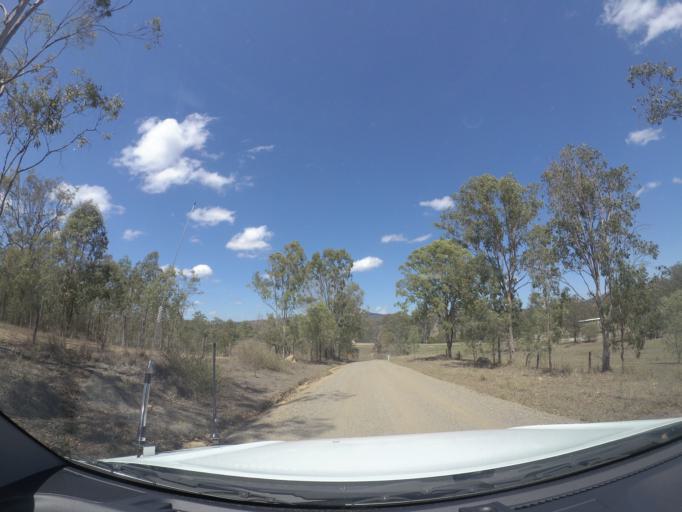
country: AU
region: Queensland
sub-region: Logan
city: Cedar Vale
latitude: -27.8489
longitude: 152.8956
